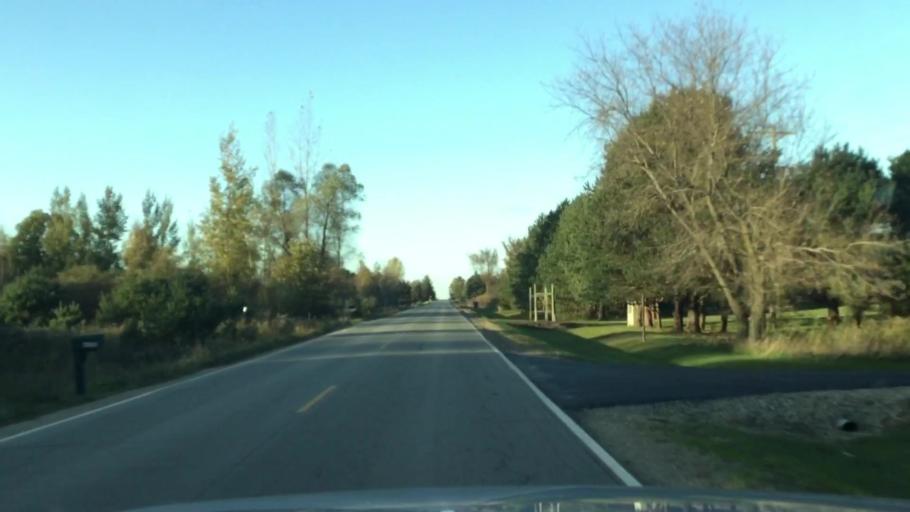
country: US
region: Michigan
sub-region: Sanilac County
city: Marlette
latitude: 43.3355
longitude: -83.1837
